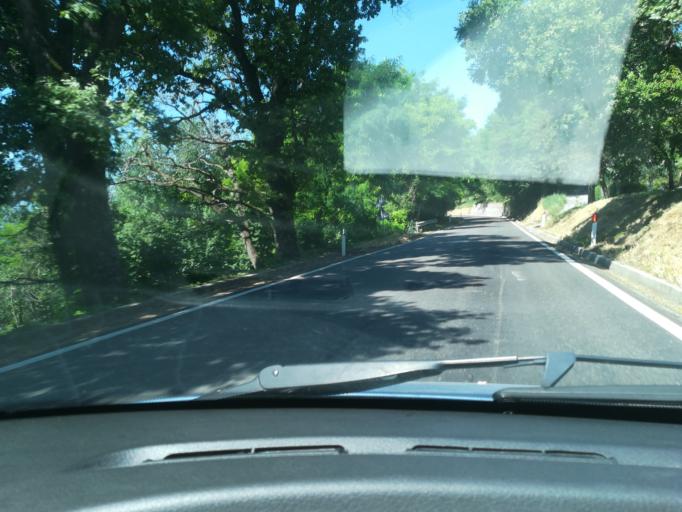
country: IT
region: The Marches
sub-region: Provincia di Macerata
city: San Ginesio
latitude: 43.1064
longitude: 13.3293
